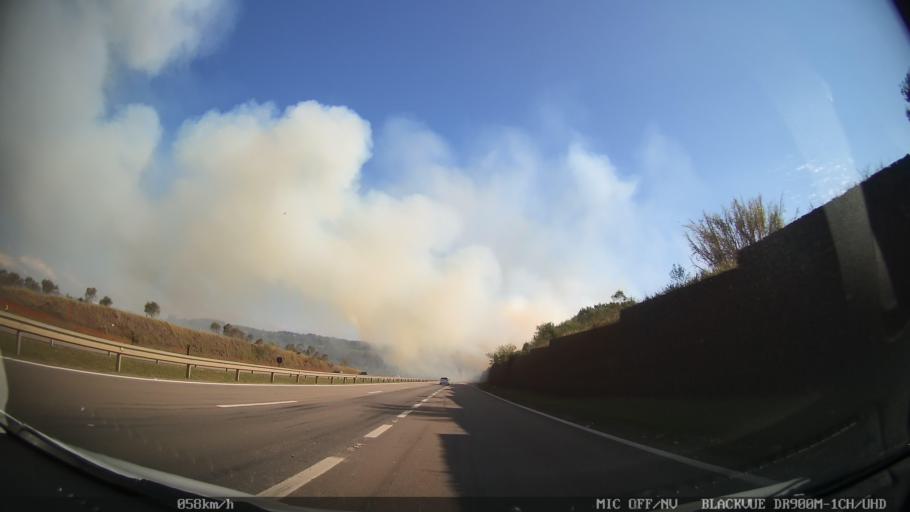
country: BR
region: Sao Paulo
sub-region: Piracicaba
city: Piracicaba
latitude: -22.6944
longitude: -47.6030
